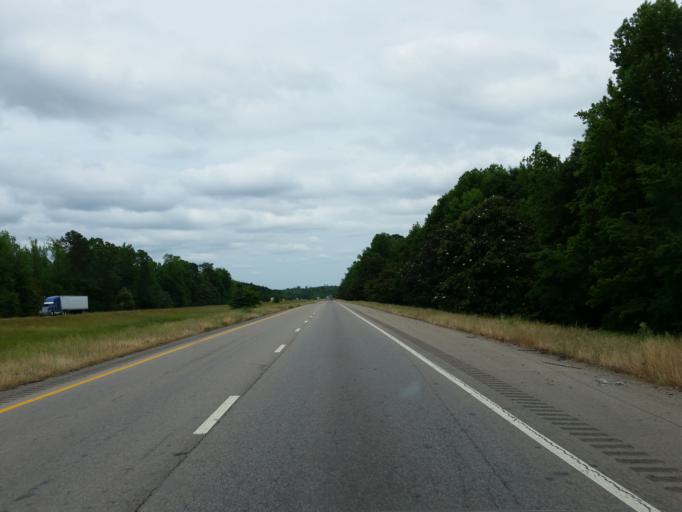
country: US
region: Mississippi
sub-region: Lauderdale County
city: Marion
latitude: 32.4128
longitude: -88.4928
